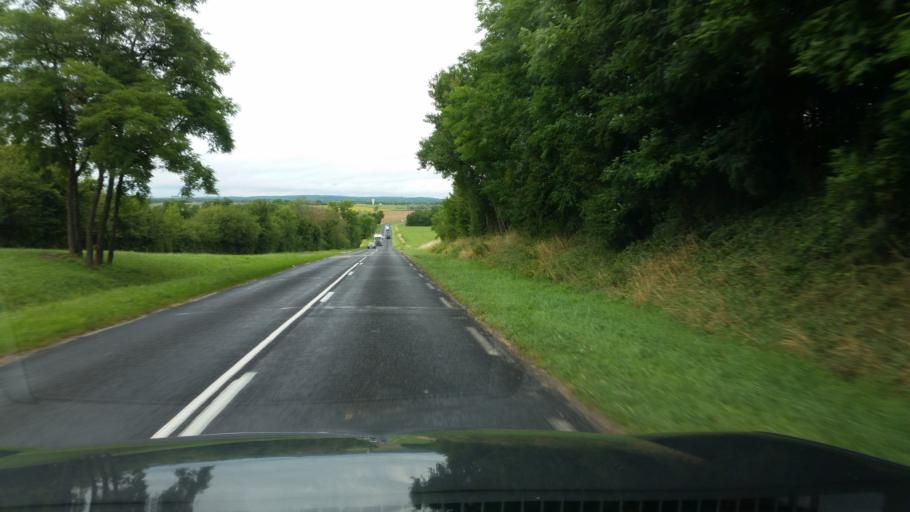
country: FR
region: Lorraine
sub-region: Departement de Meurthe-et-Moselle
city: Toul
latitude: 48.7191
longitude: 5.9244
